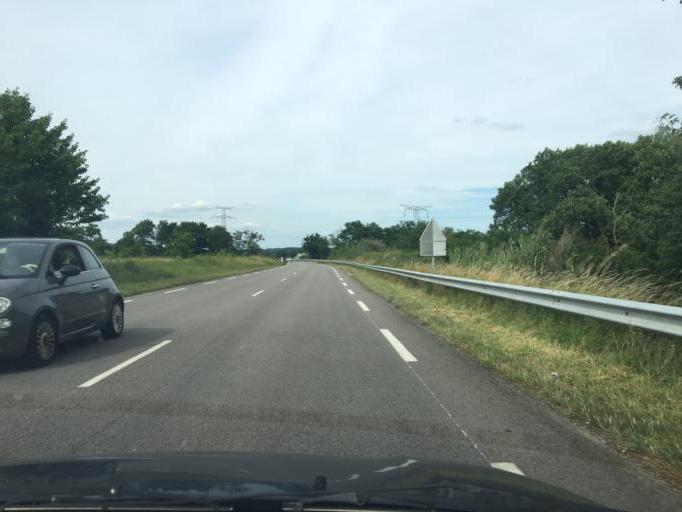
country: FR
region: Rhone-Alpes
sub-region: Departement de la Drome
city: Chateauneuf-sur-Isere
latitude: 45.0344
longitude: 4.9333
